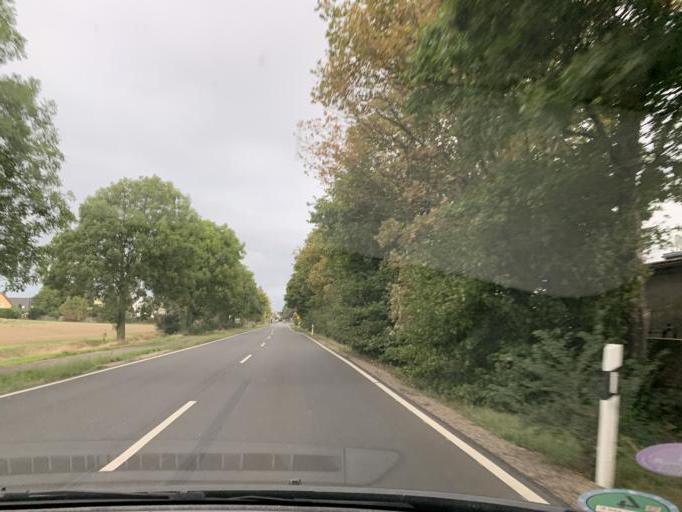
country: DE
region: North Rhine-Westphalia
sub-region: Regierungsbezirk Koln
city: Dueren
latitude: 50.8256
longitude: 6.4419
